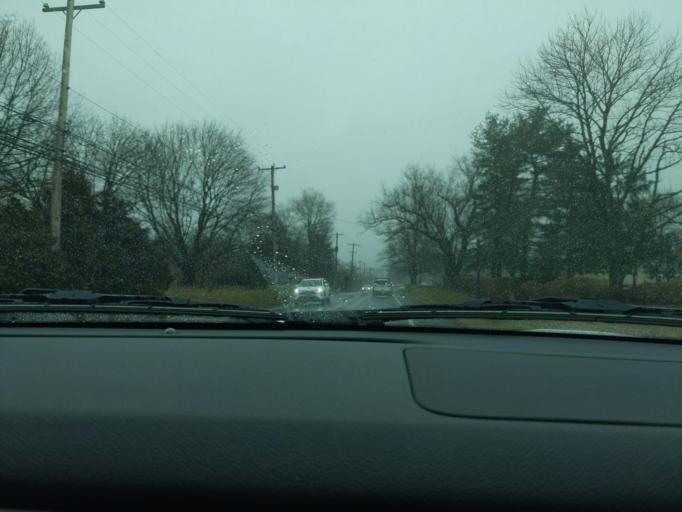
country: US
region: Pennsylvania
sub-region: Bucks County
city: Dublin
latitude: 40.3520
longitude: -75.1691
